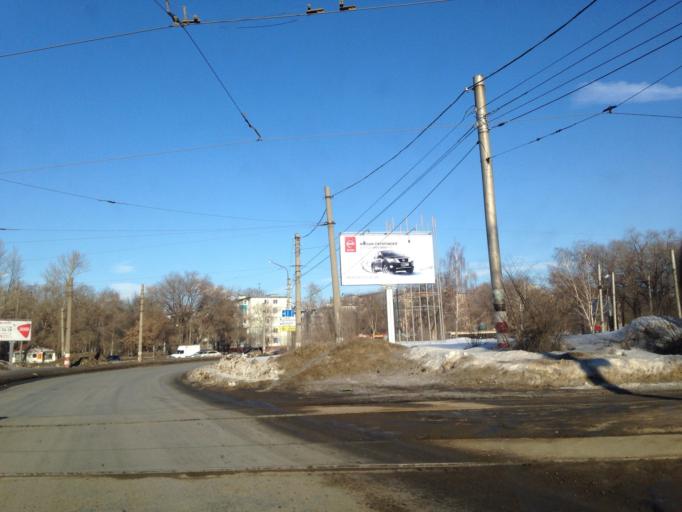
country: RU
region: Ulyanovsk
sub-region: Ulyanovskiy Rayon
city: Ulyanovsk
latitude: 54.2976
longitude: 48.3214
